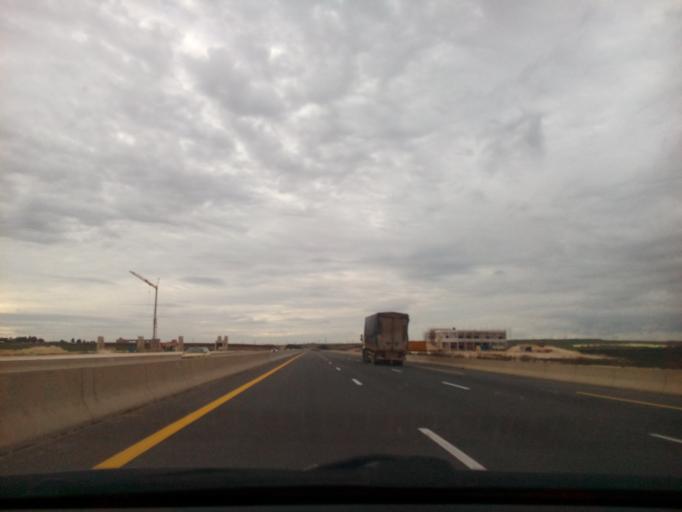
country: DZ
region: Mascara
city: Sig
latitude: 35.5420
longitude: -0.3520
